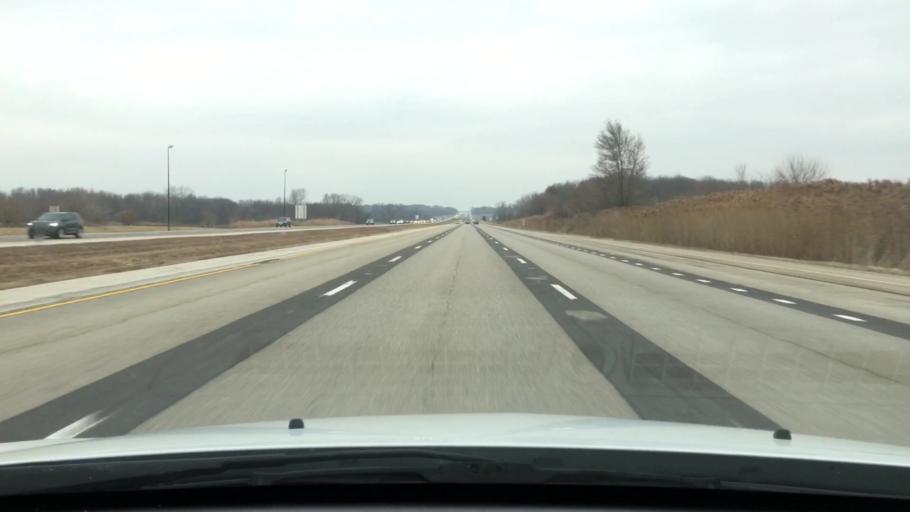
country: US
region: Illinois
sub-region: Logan County
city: Lincoln
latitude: 40.1167
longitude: -89.4164
